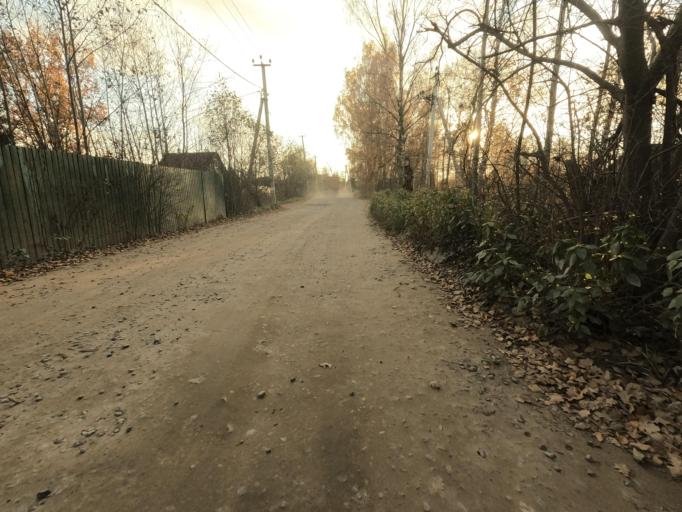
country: RU
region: St.-Petersburg
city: Beloostrov
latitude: 60.1796
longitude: 30.0407
